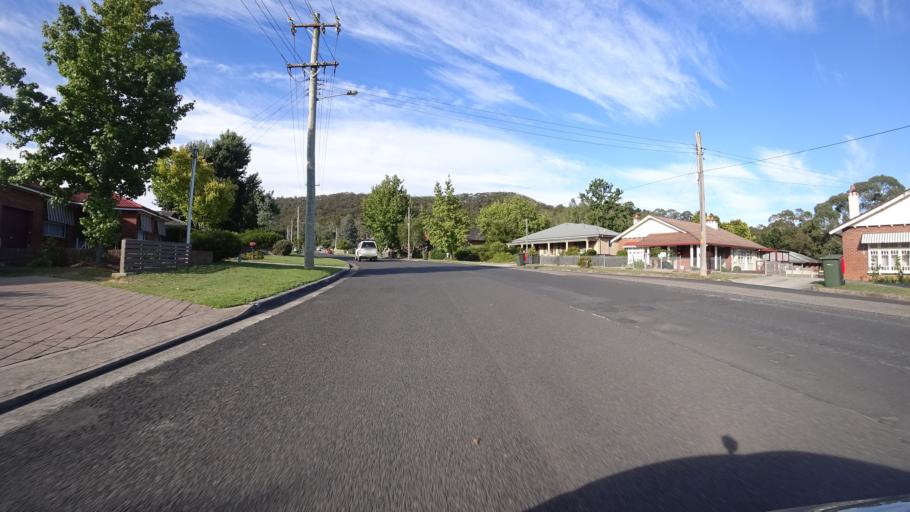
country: AU
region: New South Wales
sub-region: Lithgow
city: Lithgow
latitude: -33.4894
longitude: 150.1511
